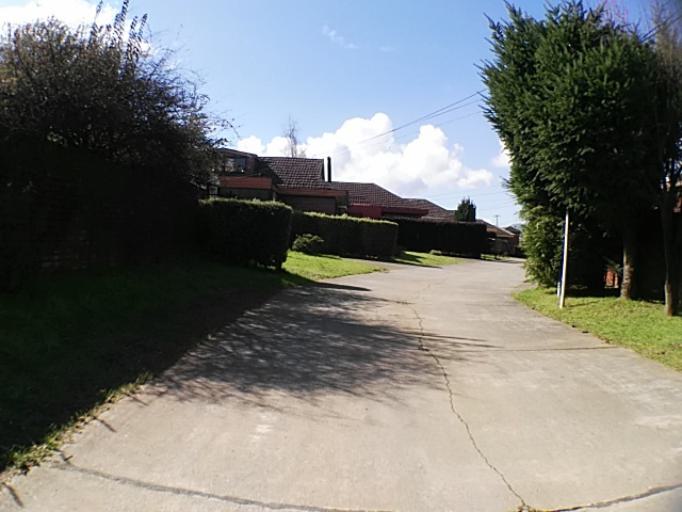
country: CL
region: Los Rios
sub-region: Provincia de Valdivia
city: Valdivia
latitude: -39.8338
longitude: -73.2301
